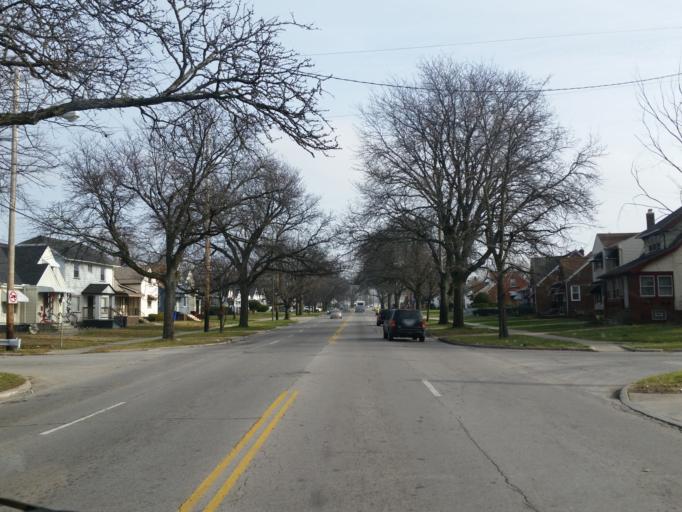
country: US
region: Ohio
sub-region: Cuyahoga County
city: Maple Heights
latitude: 41.4494
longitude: -81.5780
